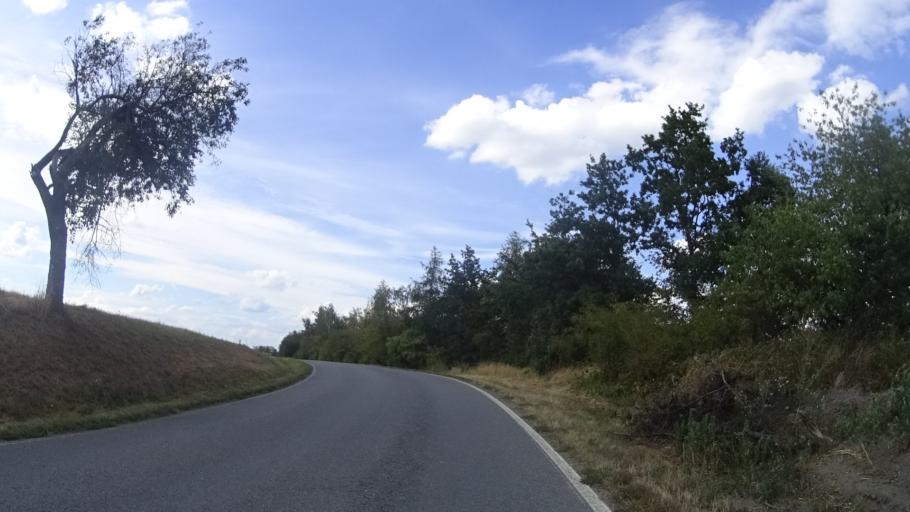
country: CZ
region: Olomoucky
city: Bila Lhota
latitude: 49.7316
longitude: 16.9800
